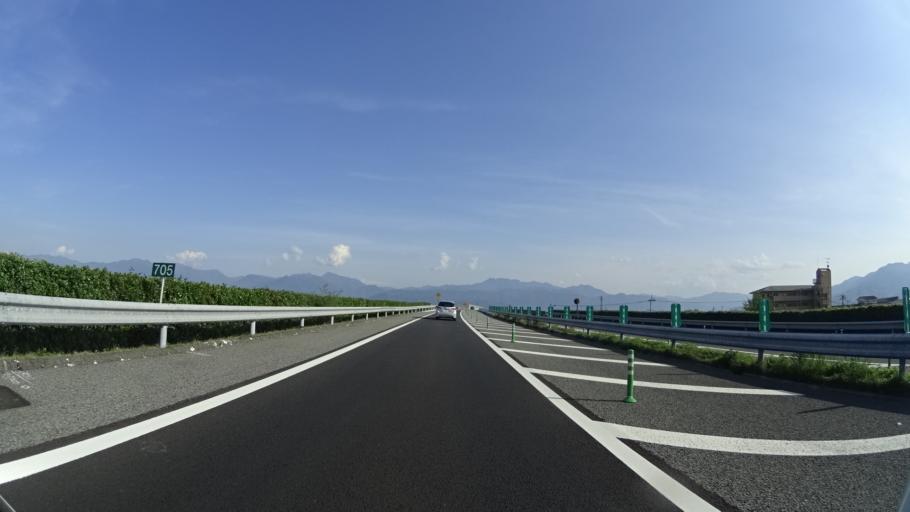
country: JP
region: Ehime
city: Saijo
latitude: 33.9536
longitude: 133.0684
